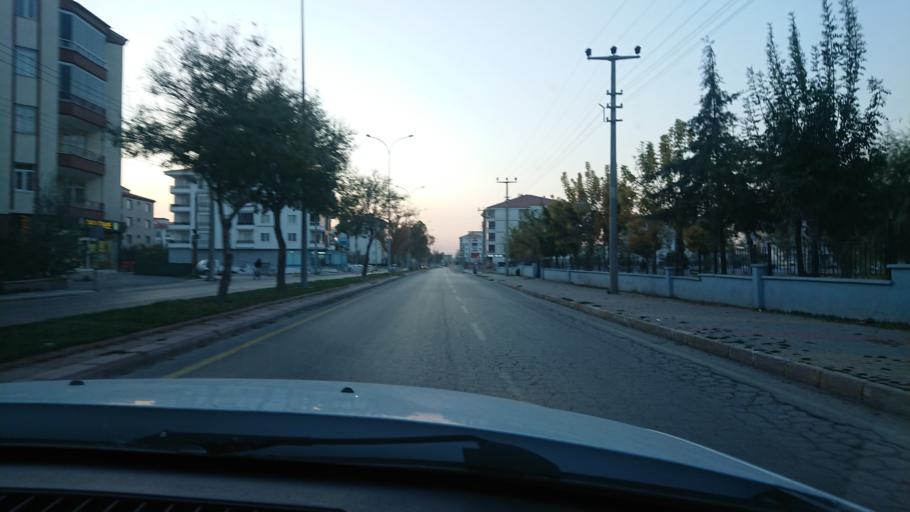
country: TR
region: Aksaray
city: Aksaray
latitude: 38.3601
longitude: 34.0073
